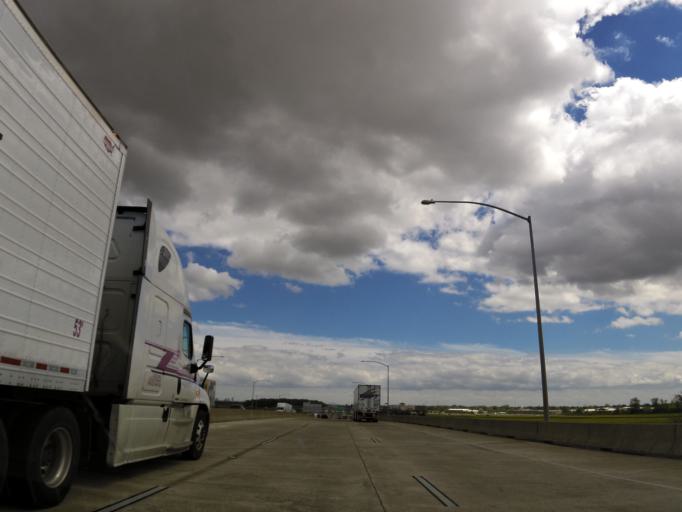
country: US
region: Arkansas
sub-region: Crittenden County
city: West Memphis
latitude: 35.1684
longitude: -90.1847
